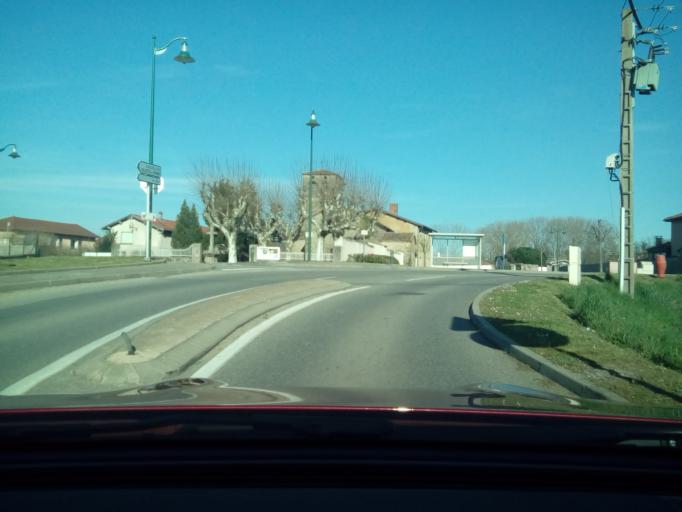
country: FR
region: Rhone-Alpes
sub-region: Departement de l'Isere
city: Serpaize
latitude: 45.5625
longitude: 4.9158
